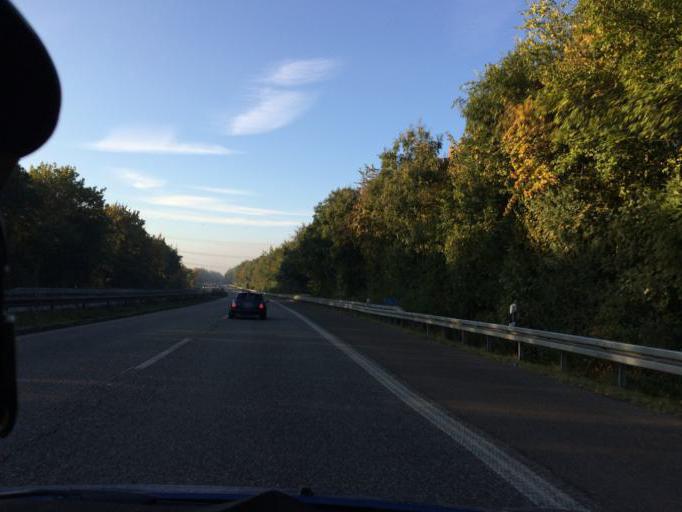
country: DE
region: North Rhine-Westphalia
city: Meckenheim
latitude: 50.6130
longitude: 7.0423
